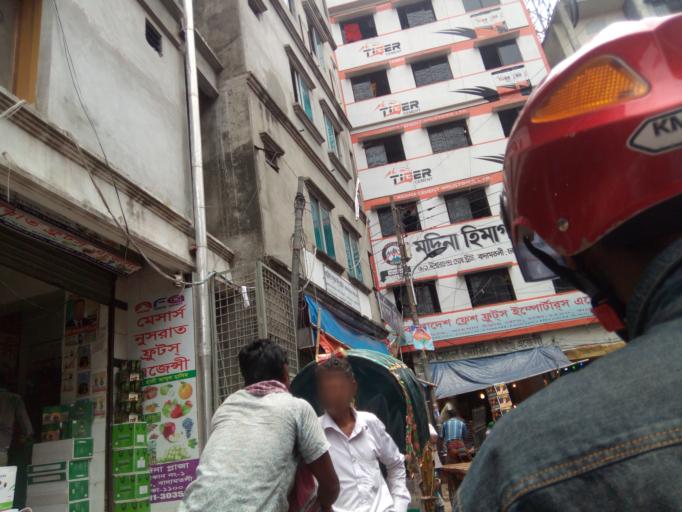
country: BD
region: Dhaka
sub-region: Dhaka
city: Dhaka
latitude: 23.7099
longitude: 90.4034
